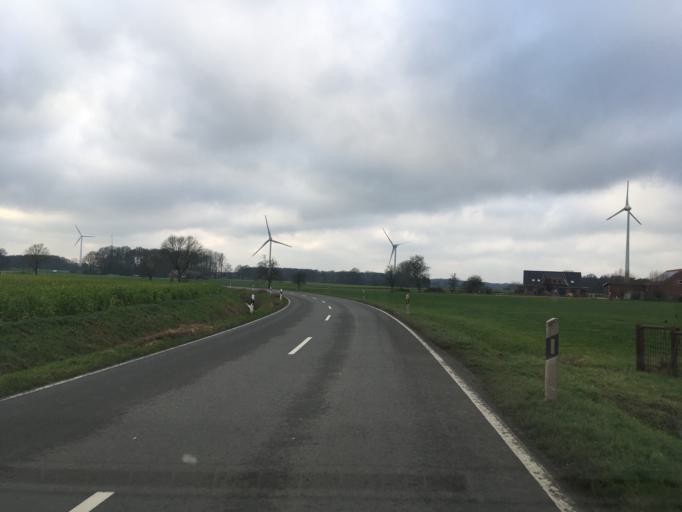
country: DE
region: North Rhine-Westphalia
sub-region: Regierungsbezirk Munster
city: Gescher
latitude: 51.9498
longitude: 6.9625
